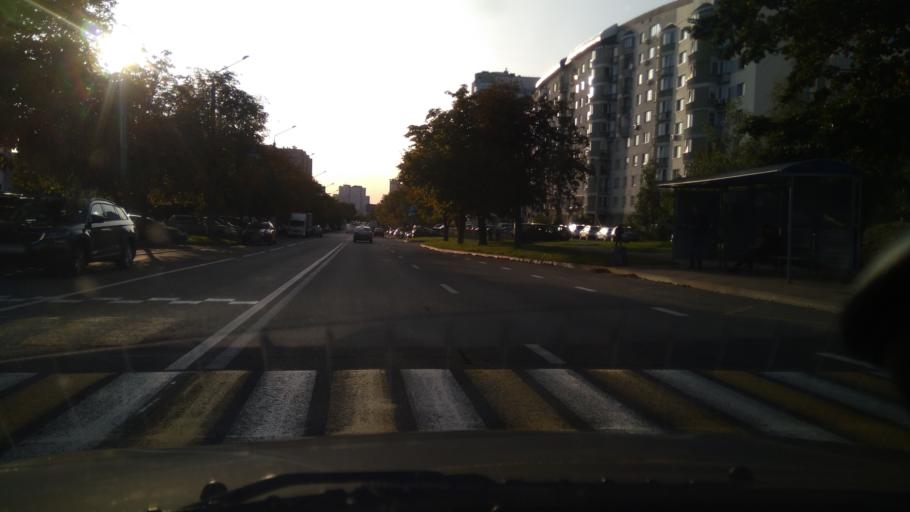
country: BY
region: Minsk
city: Novoye Medvezhino
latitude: 53.9045
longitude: 27.4518
